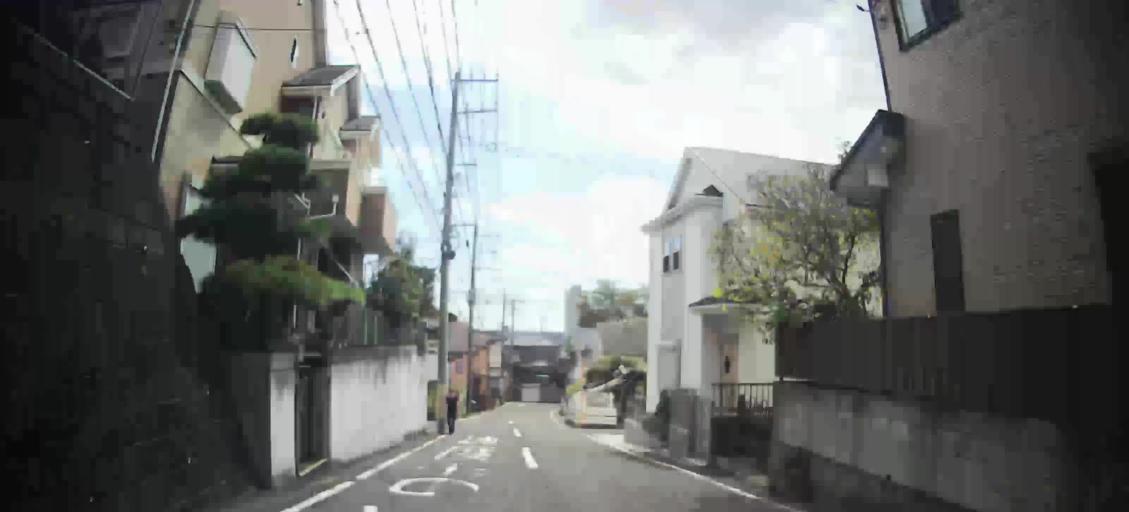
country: JP
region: Kanagawa
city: Yokohama
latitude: 35.4832
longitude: 139.5509
